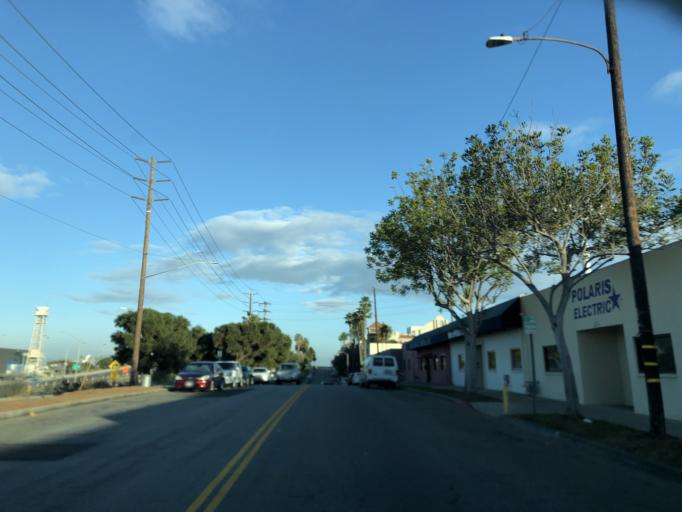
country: US
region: California
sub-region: Los Angeles County
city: El Segundo
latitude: 33.9309
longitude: -118.4033
